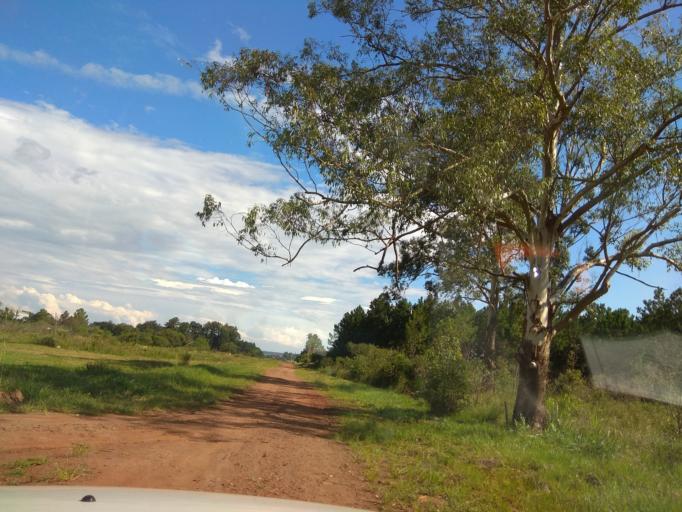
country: AR
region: Misiones
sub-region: Departamento de Candelaria
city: Candelaria
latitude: -27.4654
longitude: -55.7558
